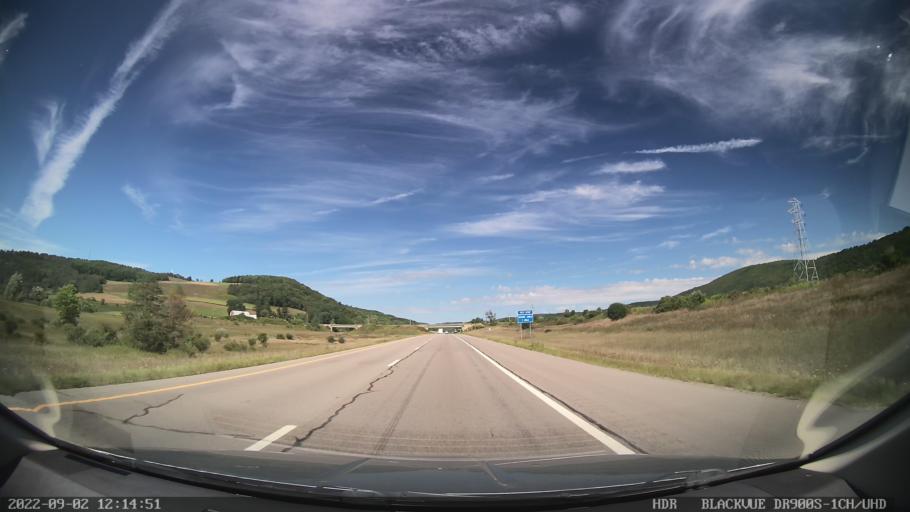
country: US
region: New York
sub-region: Steuben County
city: Wayland
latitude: 42.4588
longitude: -77.4803
